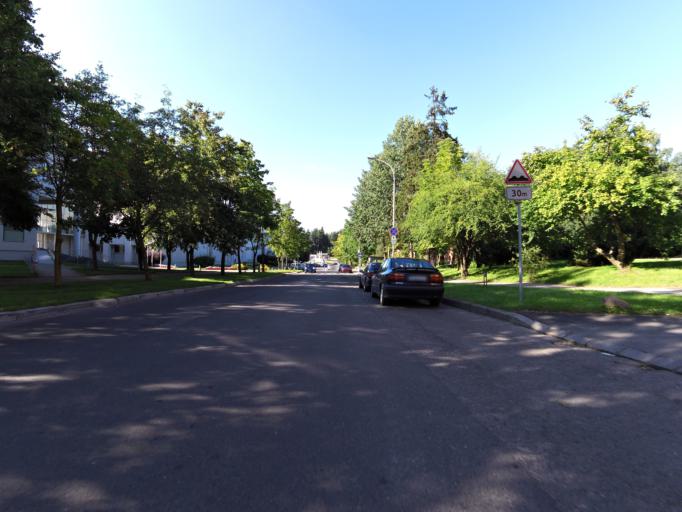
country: LT
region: Vilnius County
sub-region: Vilnius
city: Fabijoniskes
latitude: 54.7332
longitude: 25.2600
